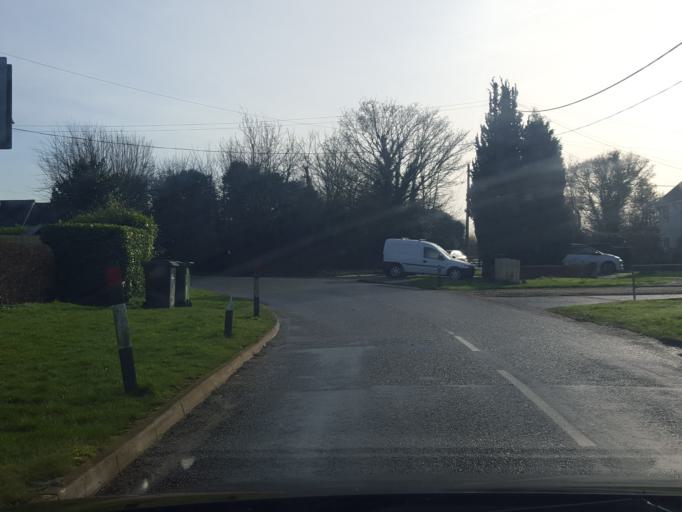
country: GB
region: England
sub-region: Suffolk
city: Sudbury
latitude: 52.0229
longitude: 0.6893
